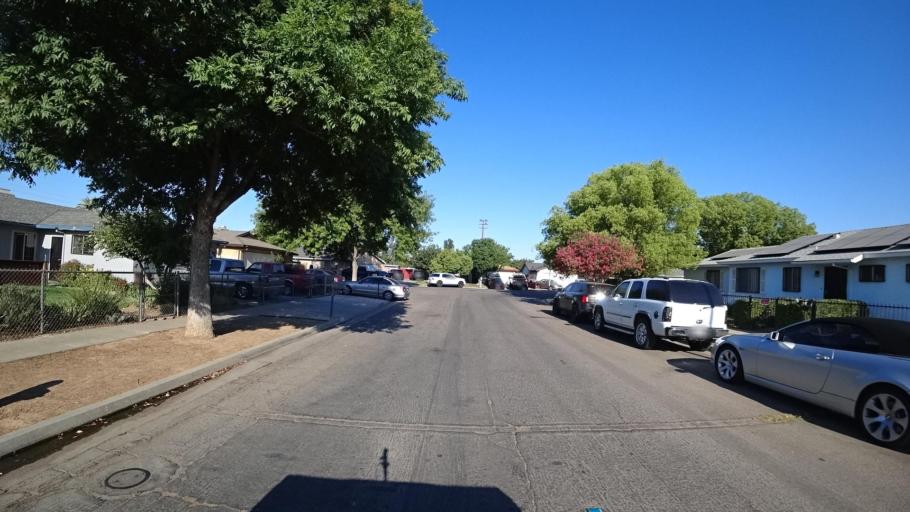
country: US
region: California
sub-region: Fresno County
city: Fresno
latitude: 36.7149
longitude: -119.7471
